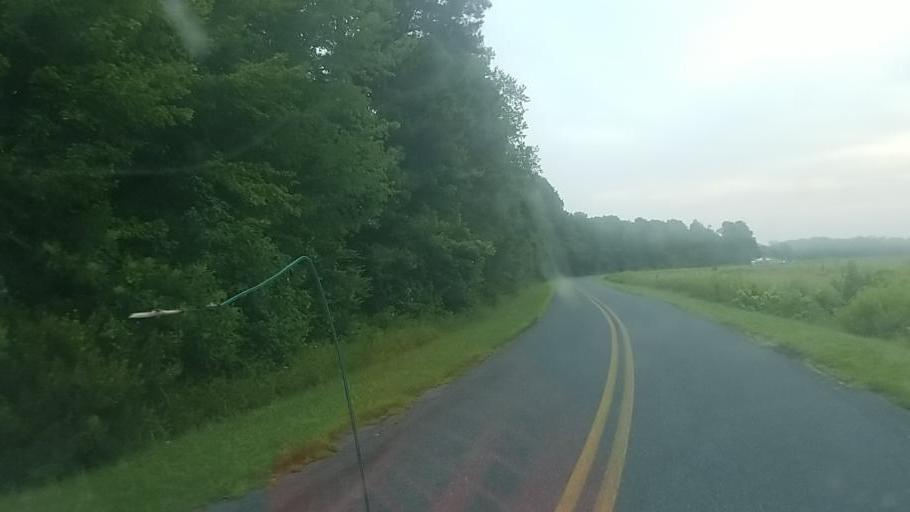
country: US
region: Maryland
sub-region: Wicomico County
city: Delmar
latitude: 38.4142
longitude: -75.4995
